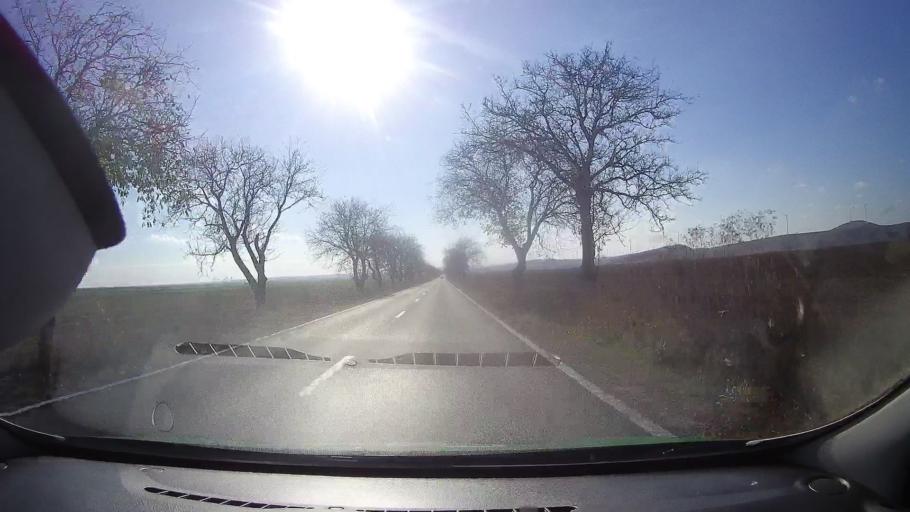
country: RO
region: Tulcea
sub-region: Comuna Ceamurlia de Jos
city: Ceamurlia de Jos
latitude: 44.7984
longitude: 28.6904
